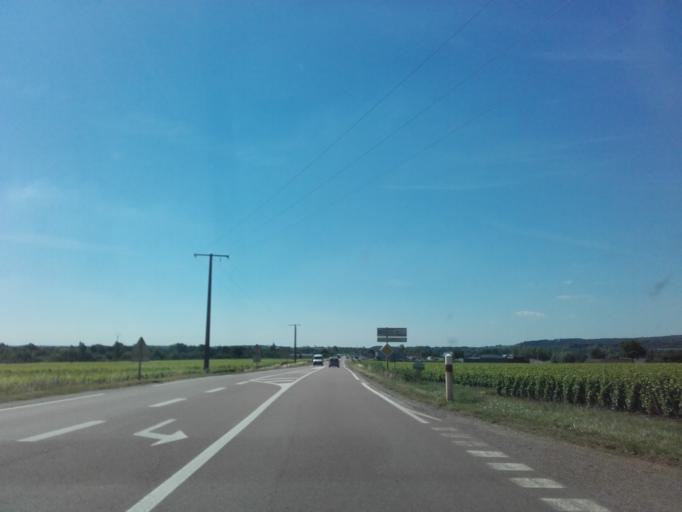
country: FR
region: Bourgogne
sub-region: Departement de la Cote-d'Or
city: Corpeau
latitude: 46.9339
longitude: 4.7390
